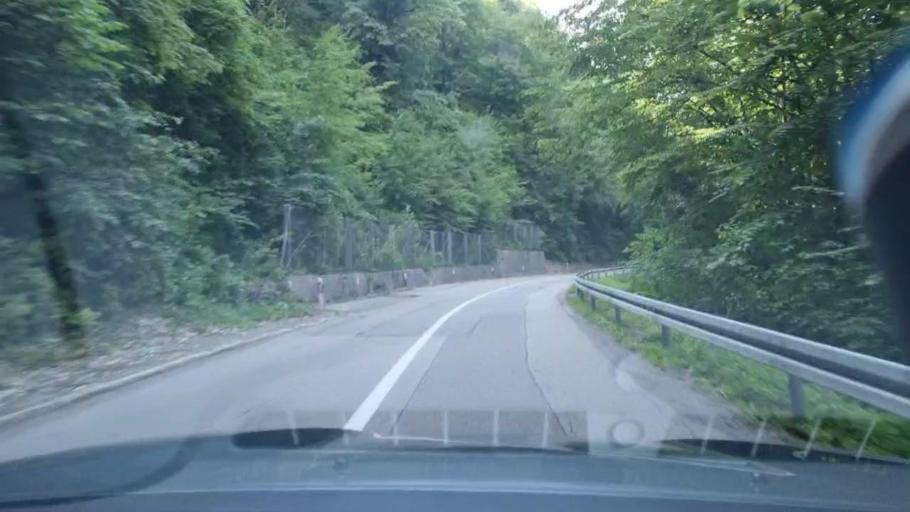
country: BA
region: Federation of Bosnia and Herzegovina
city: Bosanska Krupa
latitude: 44.8757
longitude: 16.0740
